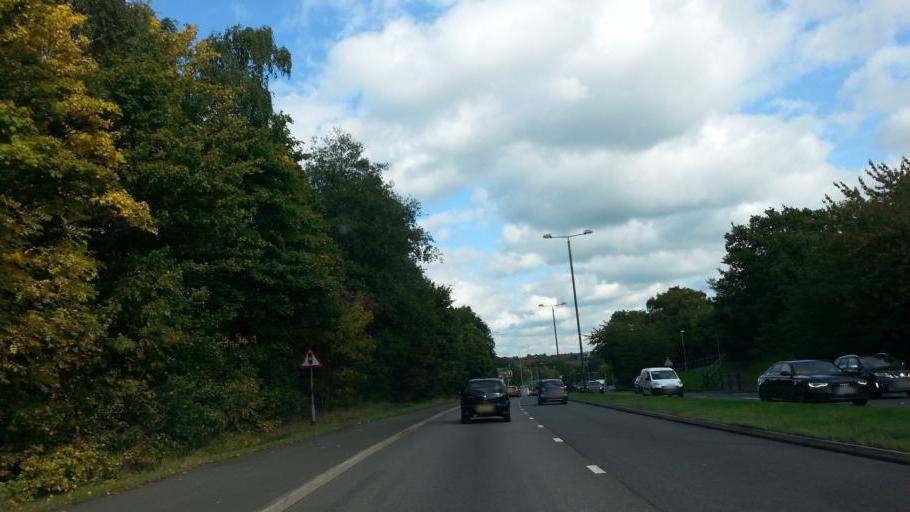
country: GB
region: England
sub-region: Derby
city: Derby
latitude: 52.9270
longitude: -1.5087
